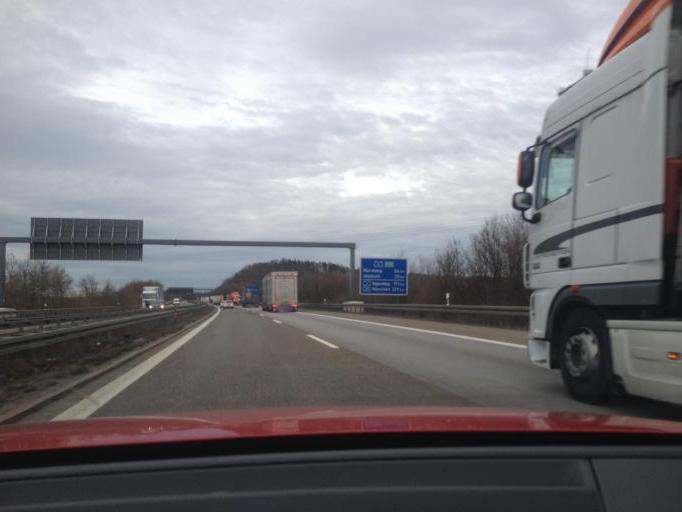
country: DE
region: Bavaria
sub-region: Regierungsbezirk Mittelfranken
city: Dombuhl
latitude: 49.2102
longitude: 10.2504
